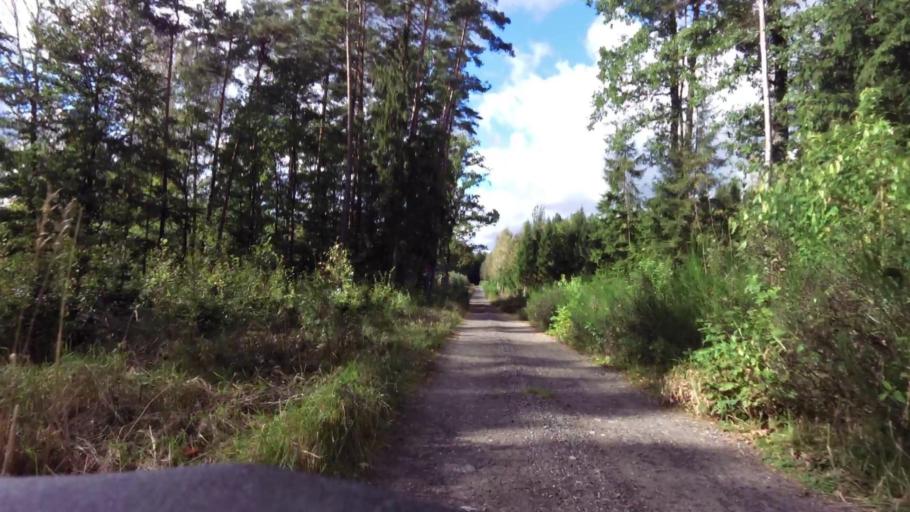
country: PL
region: West Pomeranian Voivodeship
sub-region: Koszalin
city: Koszalin
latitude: 54.0549
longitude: 16.1280
